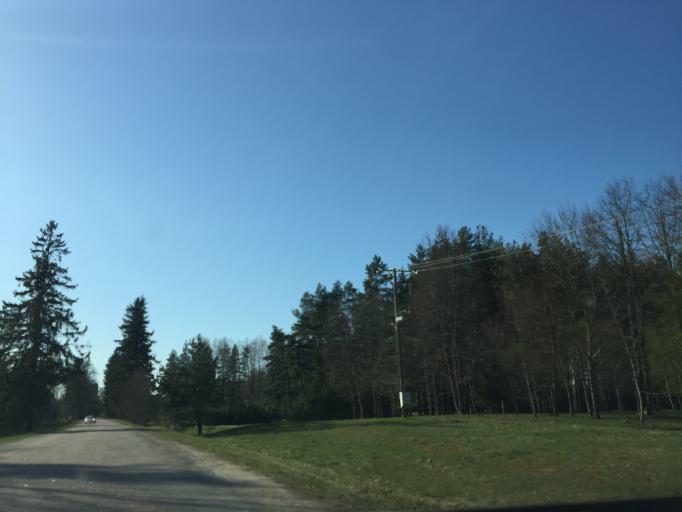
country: LV
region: Ropazu
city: Ropazi
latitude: 56.9709
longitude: 24.6470
